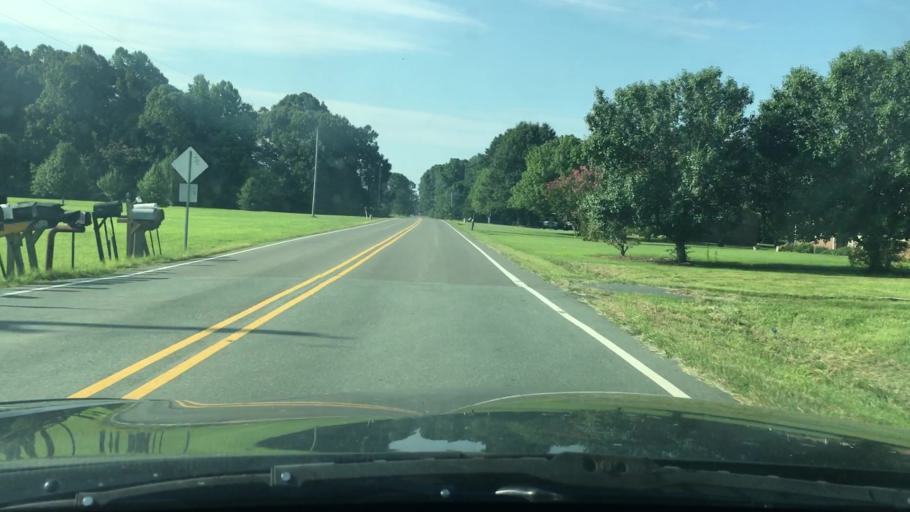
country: US
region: North Carolina
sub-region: Caswell County
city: Yanceyville
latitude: 36.2772
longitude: -79.3482
